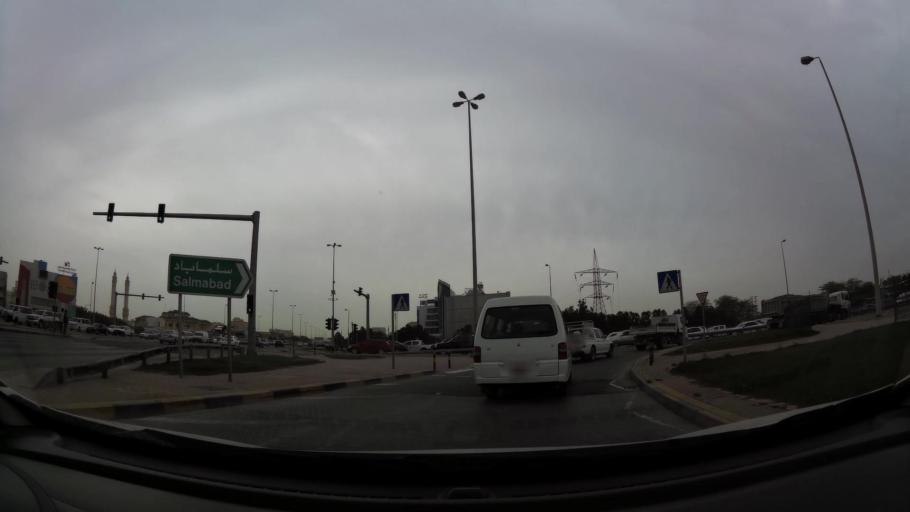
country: BH
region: Northern
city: Madinat `Isa
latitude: 26.1871
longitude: 50.5362
